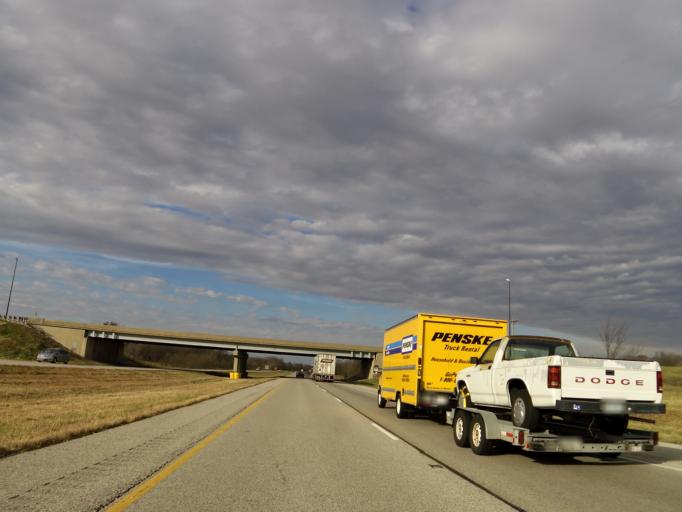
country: US
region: Illinois
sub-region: Washington County
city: Nashville
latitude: 38.3915
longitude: -89.3694
